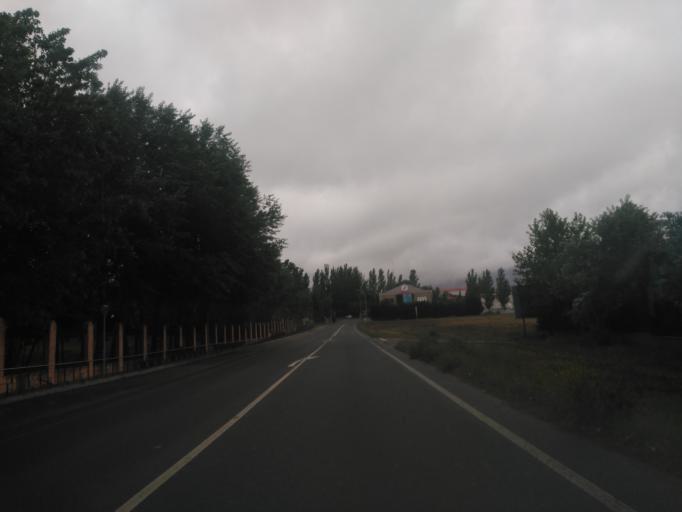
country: ES
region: Castille and Leon
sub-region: Provincia de Salamanca
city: Guijuelo
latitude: 40.5453
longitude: -5.6761
